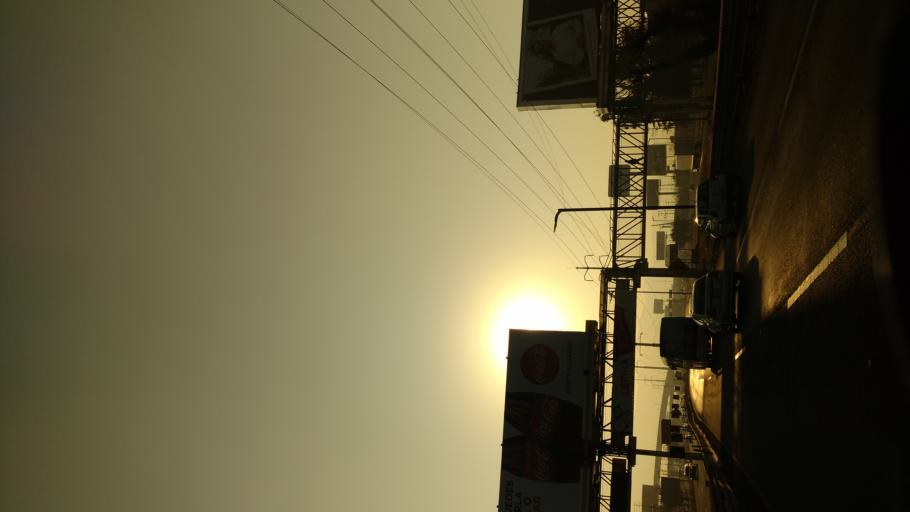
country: MX
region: Morelos
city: Lerma de Villada
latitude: 19.2849
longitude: -99.5272
